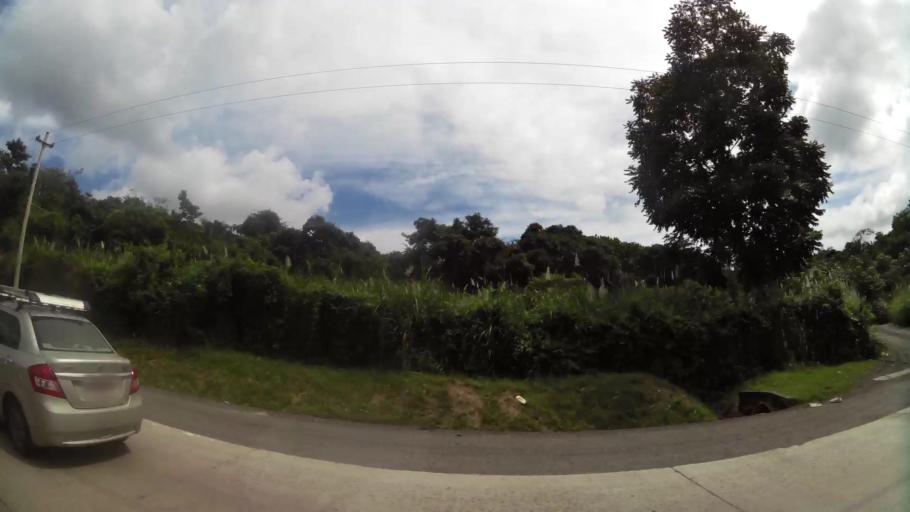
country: PA
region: Panama
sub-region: Distrito de Panama
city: Paraiso
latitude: 9.0032
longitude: -79.6495
